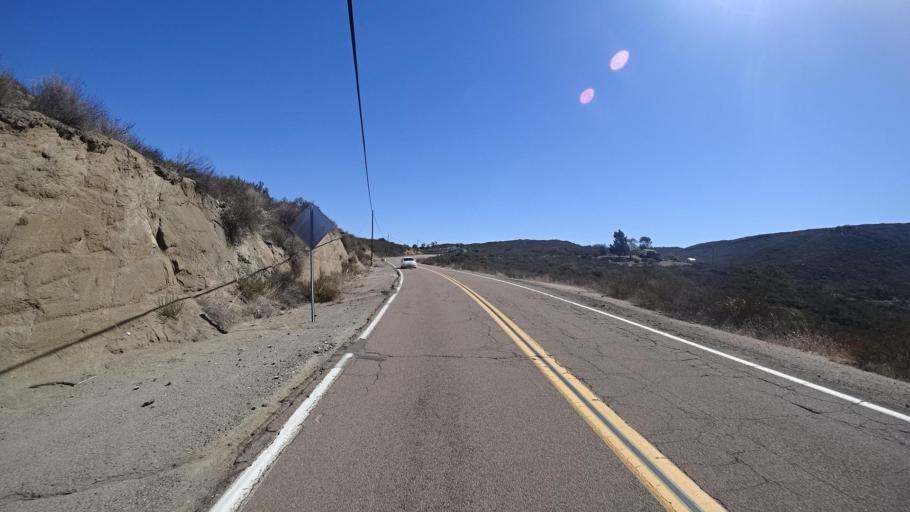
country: US
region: California
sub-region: San Diego County
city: Alpine
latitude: 32.7869
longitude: -116.7246
